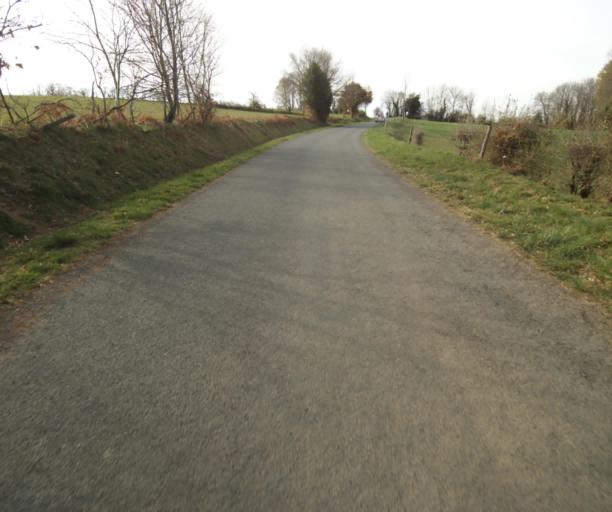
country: FR
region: Limousin
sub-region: Departement de la Correze
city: Chamboulive
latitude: 45.4158
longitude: 1.7839
